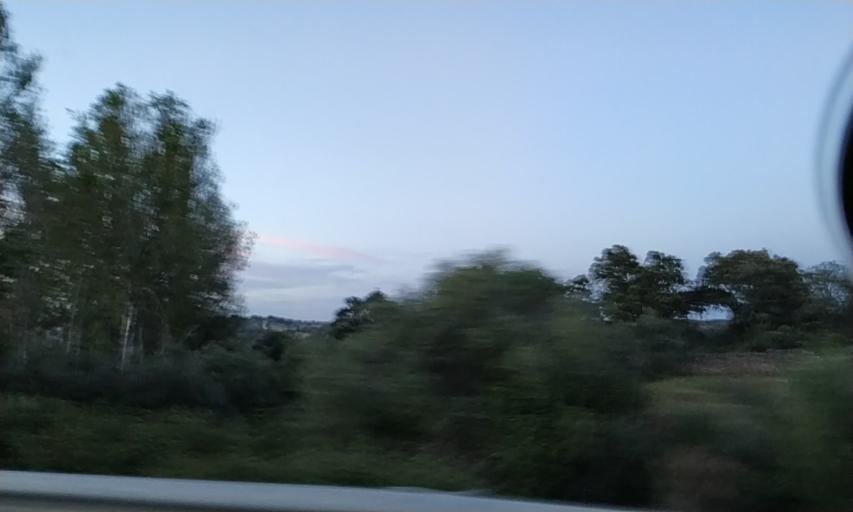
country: ES
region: Extremadura
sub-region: Provincia de Caceres
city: Piedras Albas
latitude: 39.7628
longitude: -6.9077
